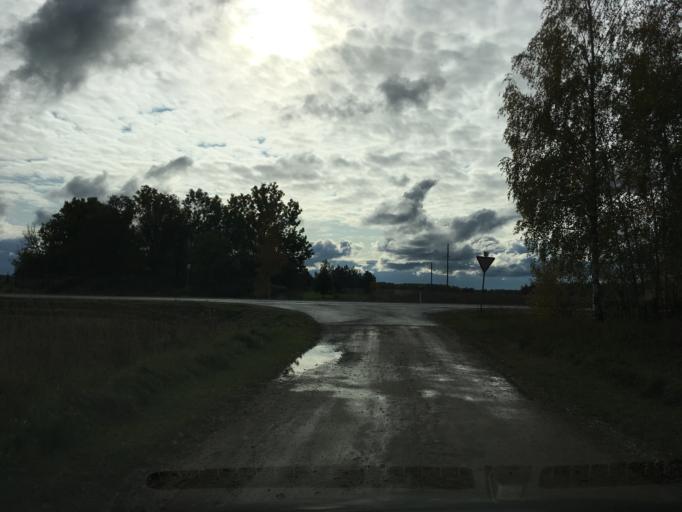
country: EE
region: Harju
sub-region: Raasiku vald
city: Raasiku
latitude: 59.2157
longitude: 25.2218
